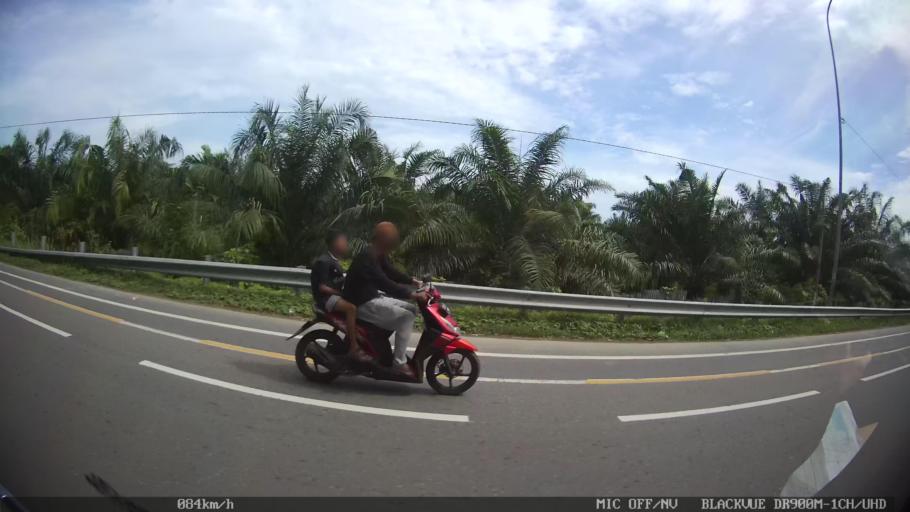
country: ID
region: North Sumatra
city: Percut
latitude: 3.5987
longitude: 98.8378
